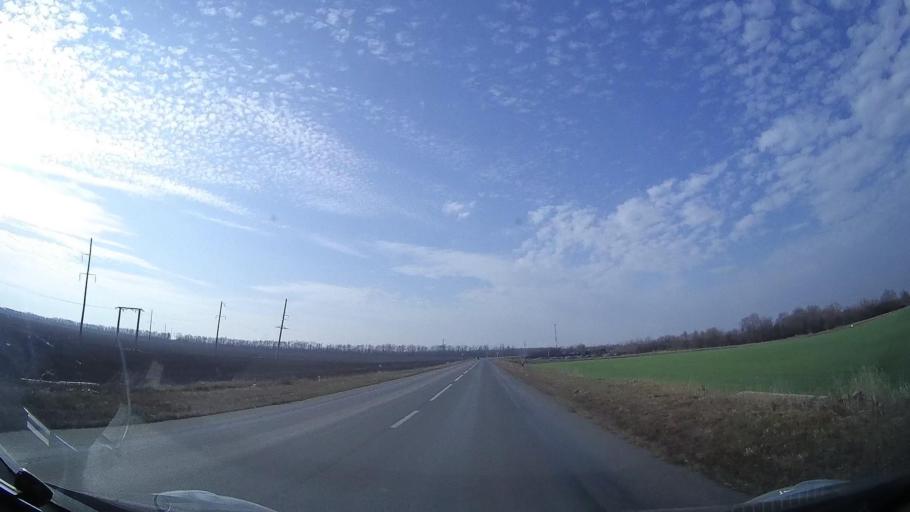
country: RU
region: Rostov
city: Veselyy
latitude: 46.9686
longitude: 40.6339
